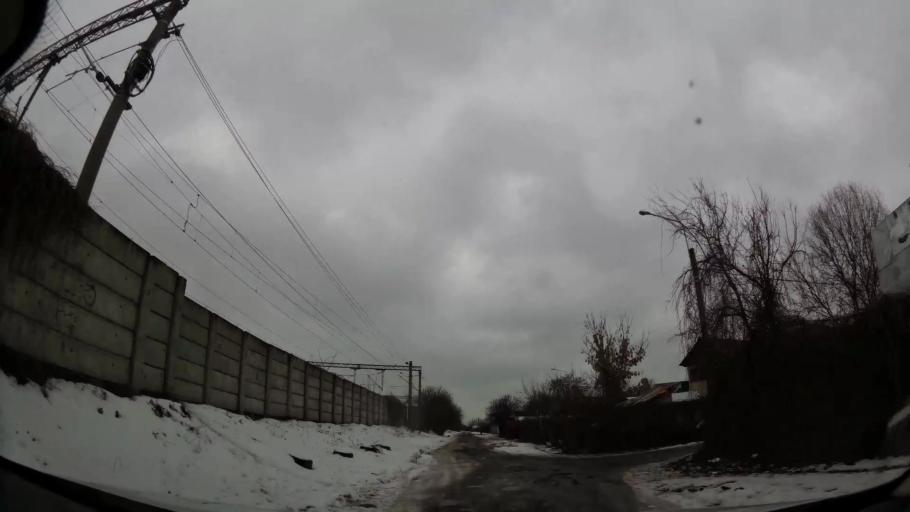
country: RO
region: Ilfov
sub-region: Comuna Chiajna
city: Rosu
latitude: 44.4816
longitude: 26.0199
